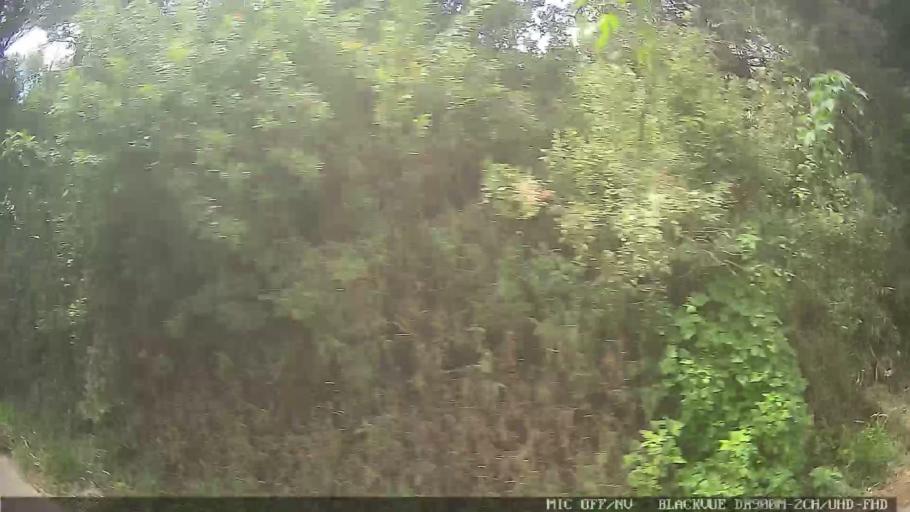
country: BR
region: Sao Paulo
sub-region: Braganca Paulista
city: Braganca Paulista
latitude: -22.8031
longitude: -46.4913
